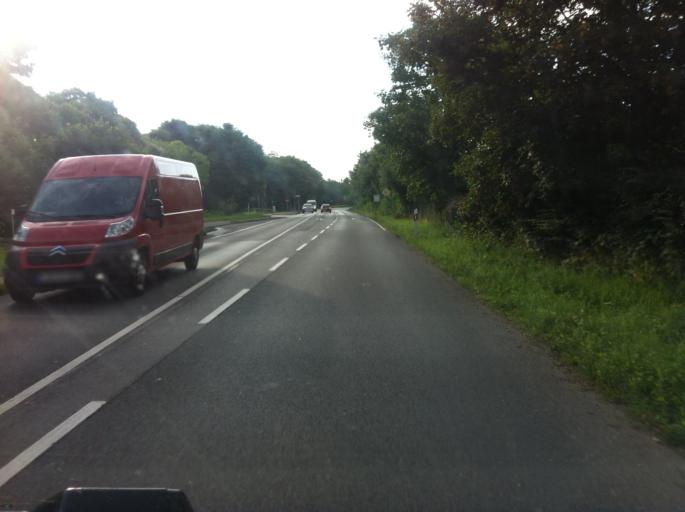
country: DE
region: North Rhine-Westphalia
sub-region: Regierungsbezirk Koln
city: Mengenich
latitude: 50.9761
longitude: 6.8572
